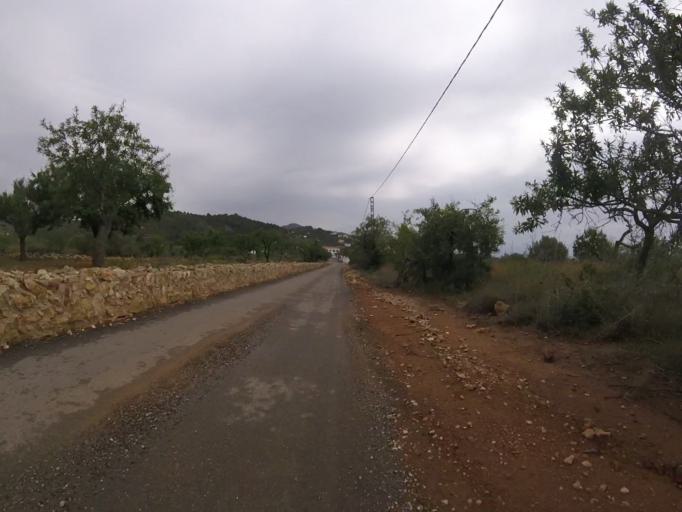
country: ES
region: Valencia
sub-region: Provincia de Castello
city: Alcoceber
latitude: 40.2460
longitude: 0.2548
